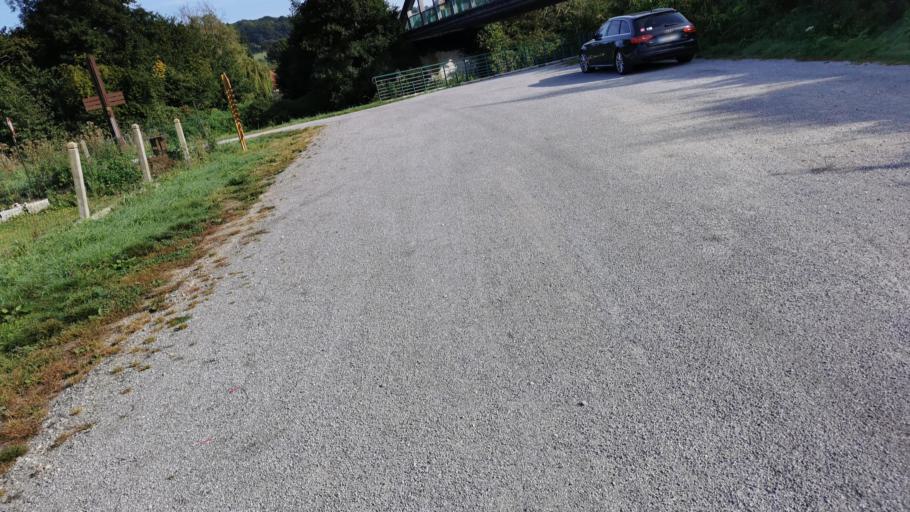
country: FR
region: Picardie
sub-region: Departement de la Somme
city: Pont-Remy
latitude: 50.0415
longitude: 1.9457
